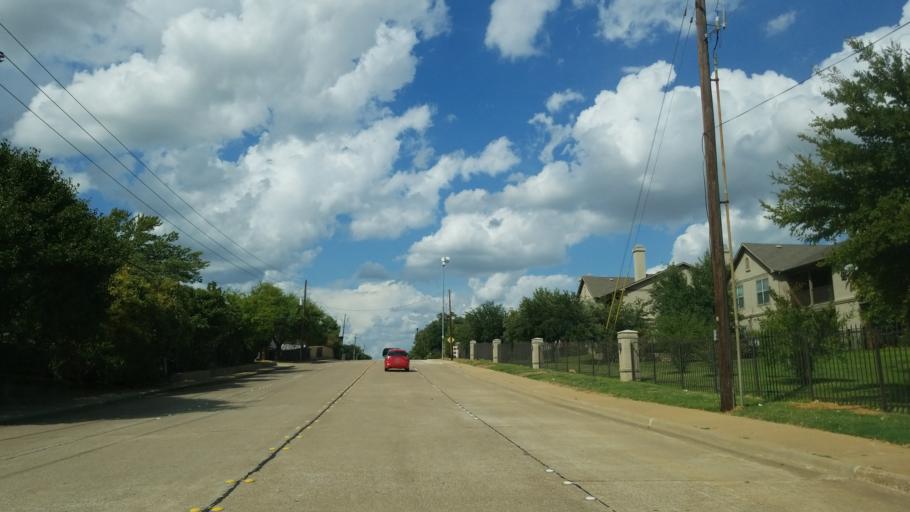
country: US
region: Texas
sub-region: Tarrant County
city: Euless
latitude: 32.8714
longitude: -97.0738
